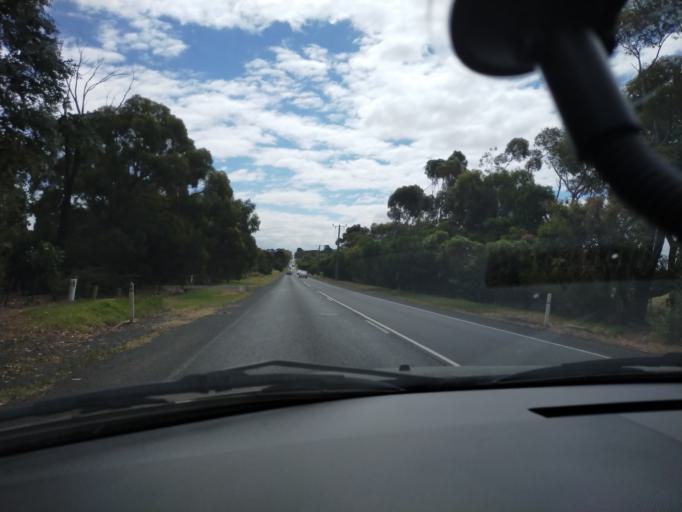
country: AU
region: Victoria
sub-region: Greater Geelong
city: Breakwater
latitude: -38.2498
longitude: 144.3435
